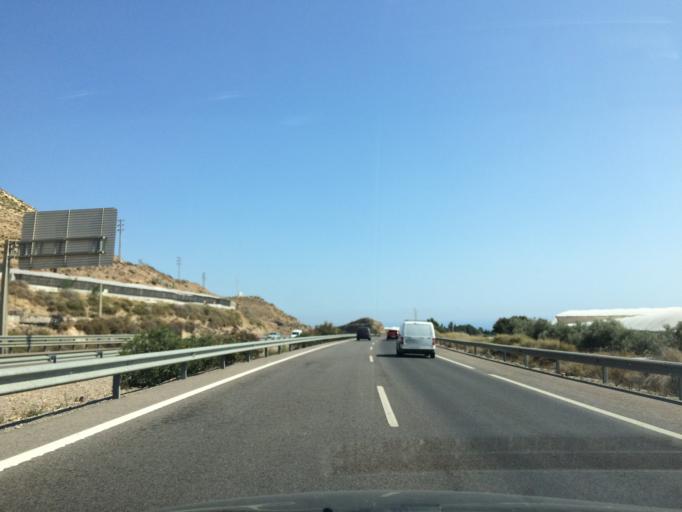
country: ES
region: Andalusia
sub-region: Provincia de Almeria
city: Vicar
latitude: 36.8128
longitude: -2.6405
